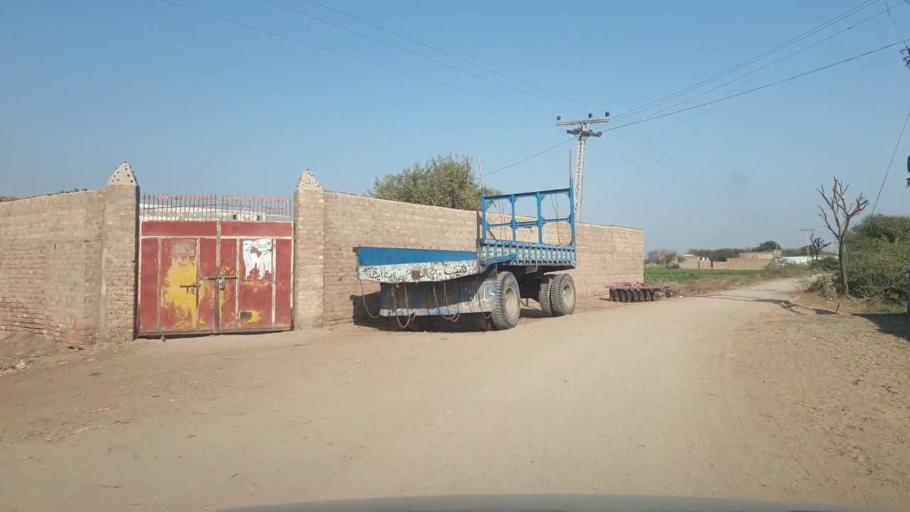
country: PK
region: Sindh
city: Chambar
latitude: 25.2882
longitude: 68.8537
